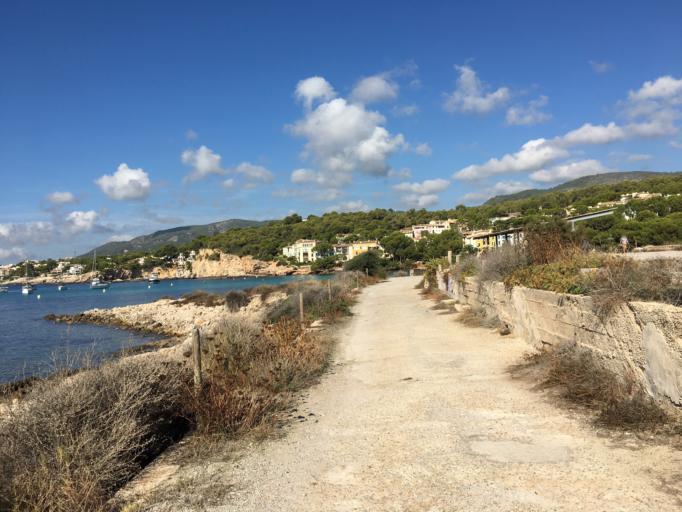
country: ES
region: Balearic Islands
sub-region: Illes Balears
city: Magaluf
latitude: 39.5317
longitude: 2.5902
